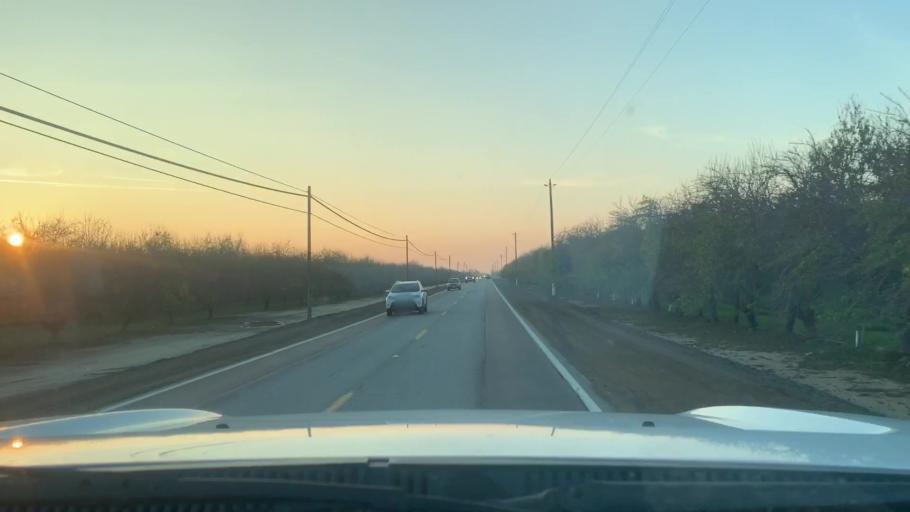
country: US
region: California
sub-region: Kern County
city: Rosedale
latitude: 35.3835
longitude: -119.2258
